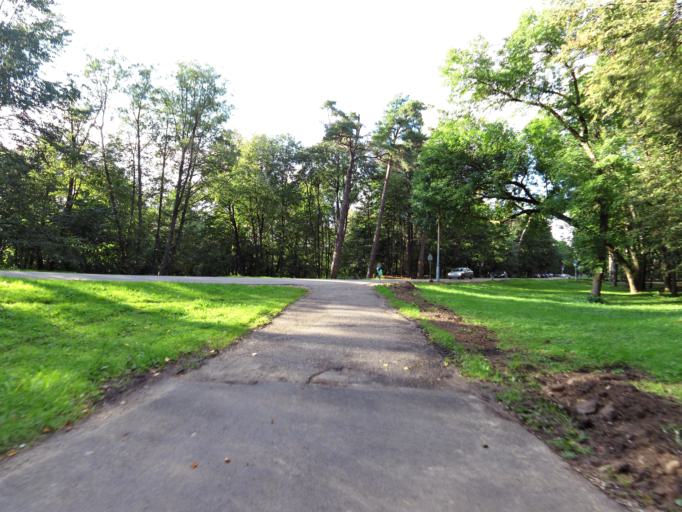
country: LT
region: Vilnius County
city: Vilkpede
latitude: 54.6806
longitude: 25.2345
